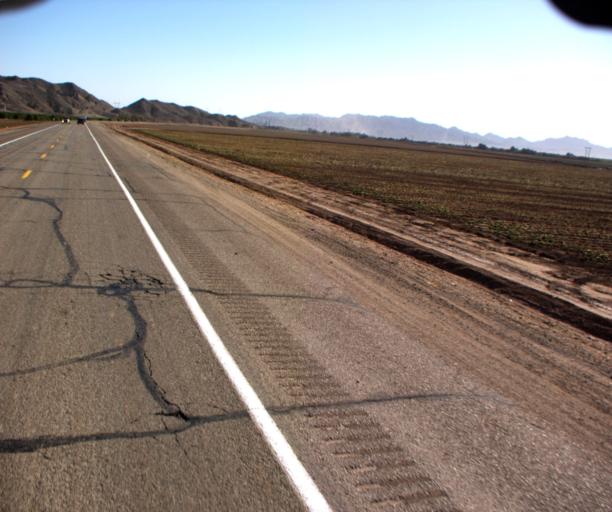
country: US
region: Arizona
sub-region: Yuma County
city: Fortuna Foothills
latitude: 32.7635
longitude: -114.4090
